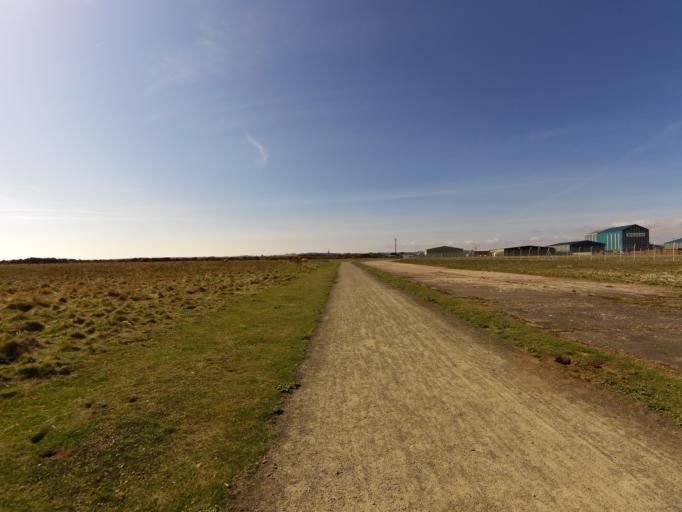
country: GB
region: Scotland
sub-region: Angus
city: Montrose
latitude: 56.7303
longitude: -2.4540
